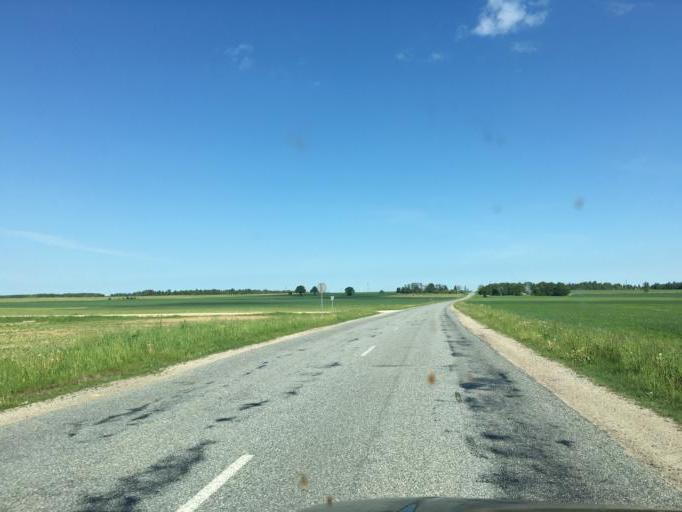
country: LV
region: Talsu Rajons
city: Valdemarpils
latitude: 57.3481
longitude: 22.4991
